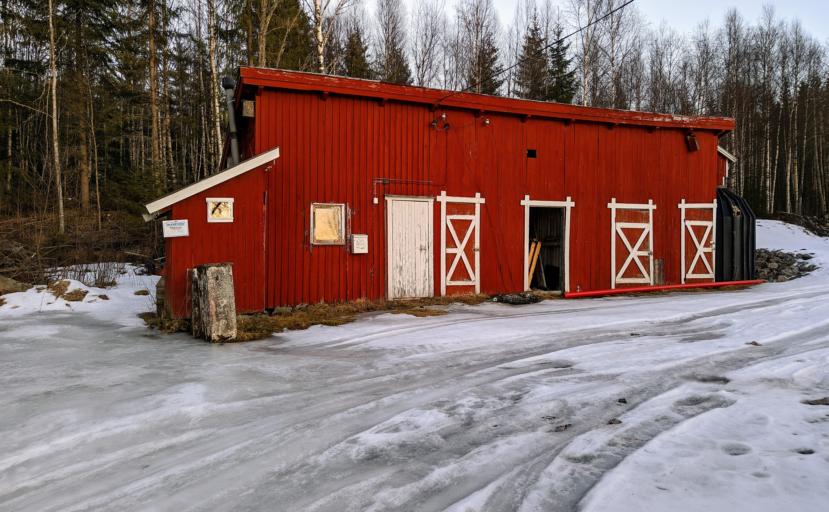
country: SE
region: Vaermland
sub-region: Eda Kommun
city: Charlottenberg
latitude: 60.1237
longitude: 12.3290
